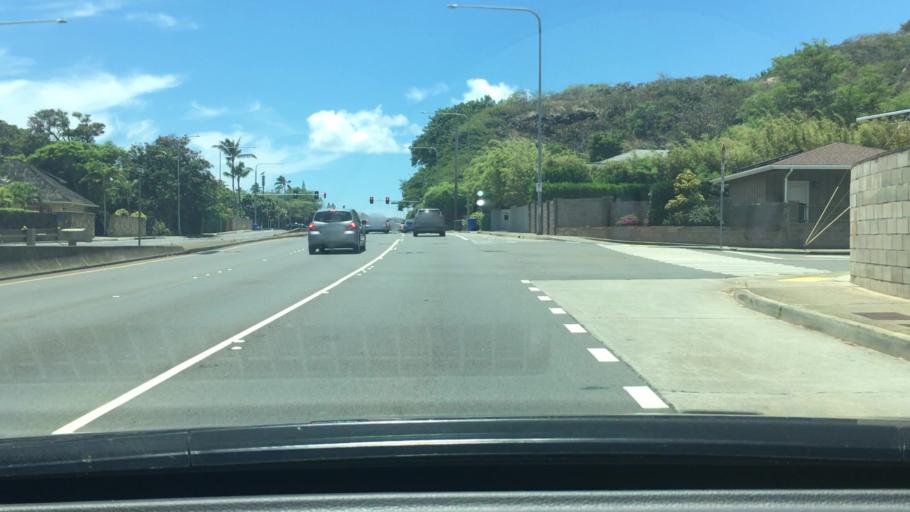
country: US
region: Hawaii
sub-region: Honolulu County
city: Waimanalo
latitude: 21.2805
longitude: -157.7428
